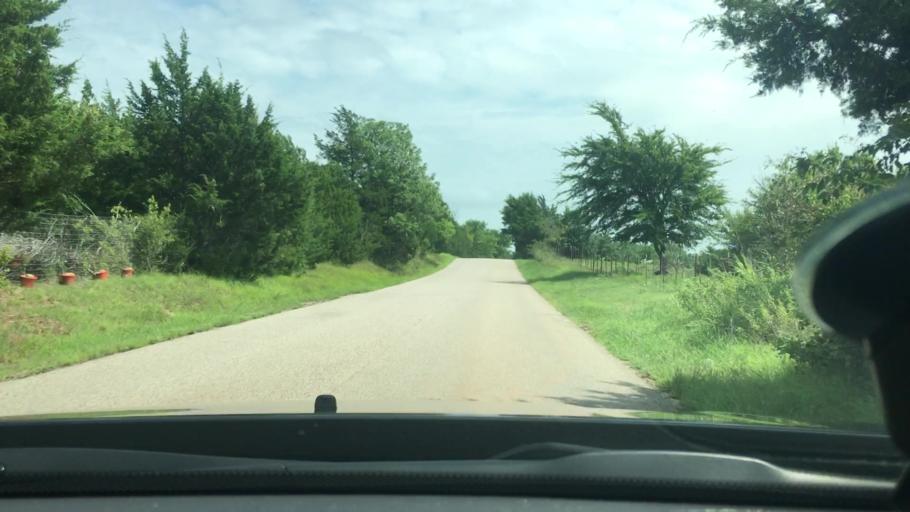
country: US
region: Oklahoma
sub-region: Pontotoc County
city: Ada
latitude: 34.8070
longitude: -96.6997
